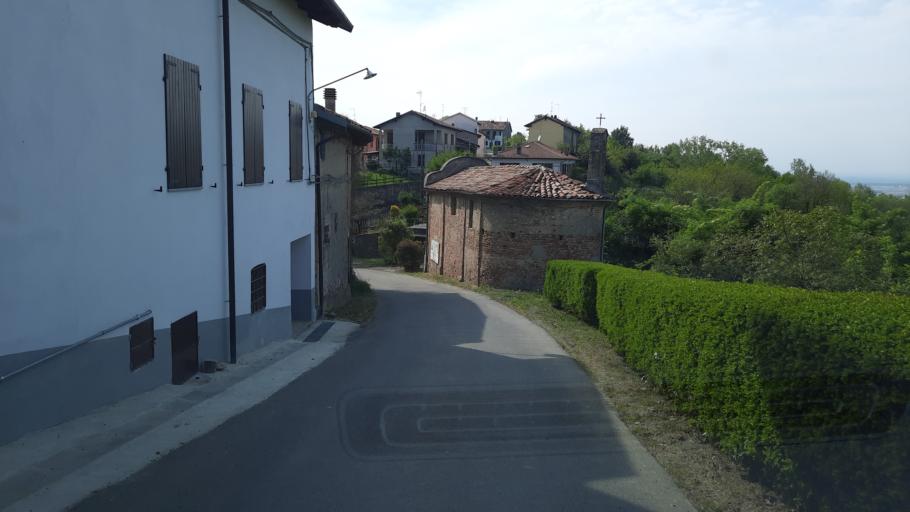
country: IT
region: Piedmont
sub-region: Provincia di Vercelli
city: Palazzolo Vercellese
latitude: 45.1682
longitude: 8.2529
